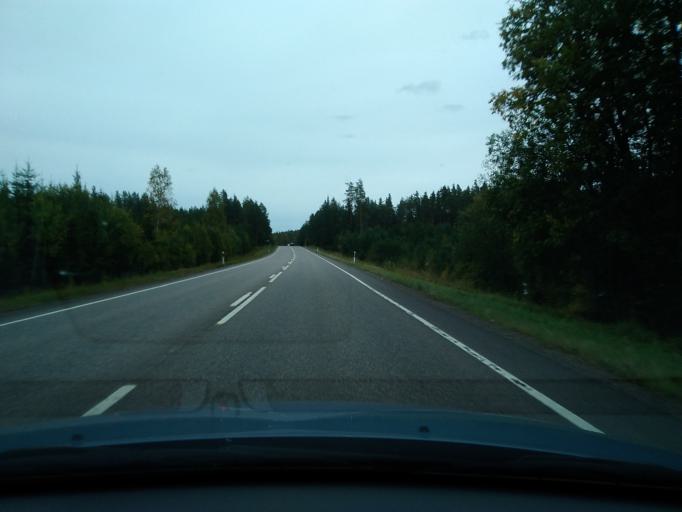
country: FI
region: Haeme
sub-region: Riihimaeki
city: Loppi
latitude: 60.7491
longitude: 24.3238
